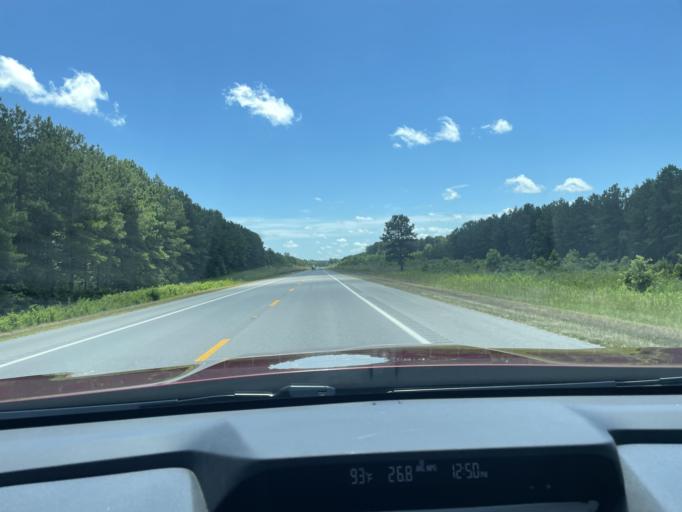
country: US
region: Arkansas
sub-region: Lincoln County
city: Star City
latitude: 33.9507
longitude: -91.9019
